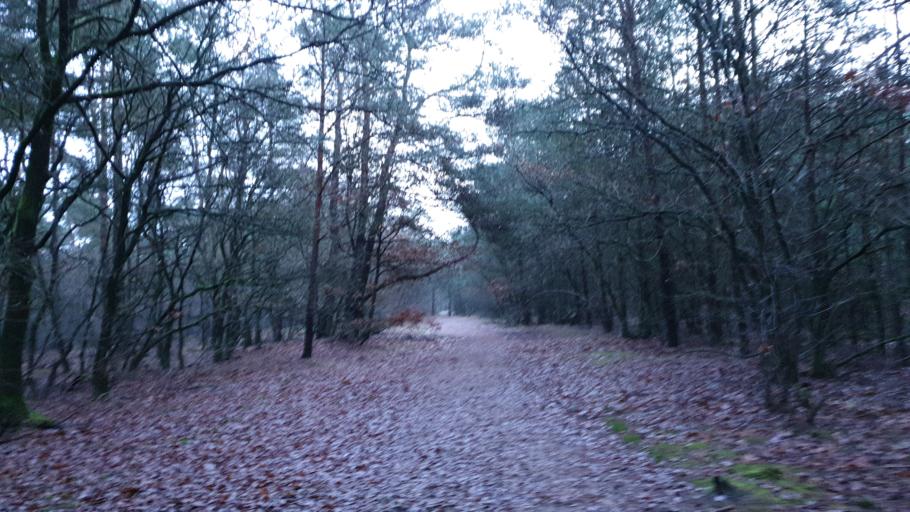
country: NL
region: Gelderland
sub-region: Gemeente Ede
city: Otterlo
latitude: 52.0990
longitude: 5.7833
